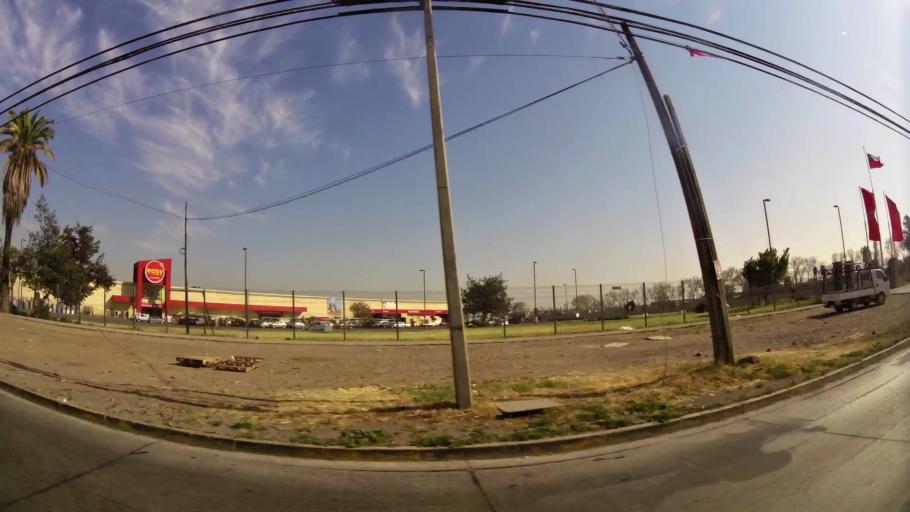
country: CL
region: Santiago Metropolitan
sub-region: Provincia de Santiago
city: Lo Prado
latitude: -33.5162
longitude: -70.7363
